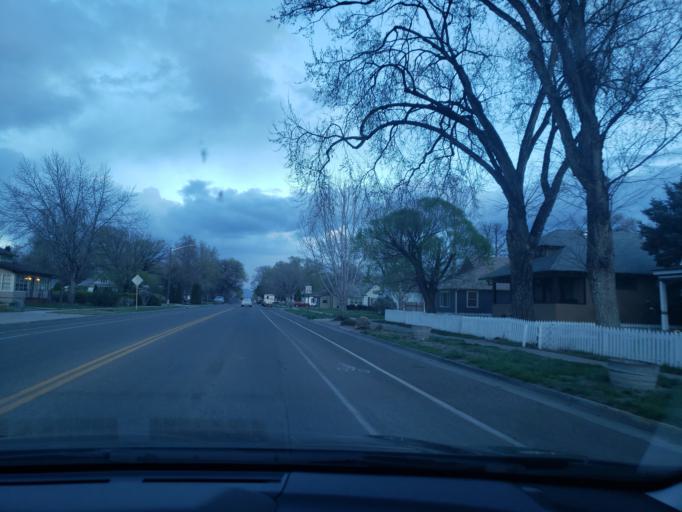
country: US
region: Colorado
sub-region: Mesa County
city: Fruita
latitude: 39.1589
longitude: -108.7289
